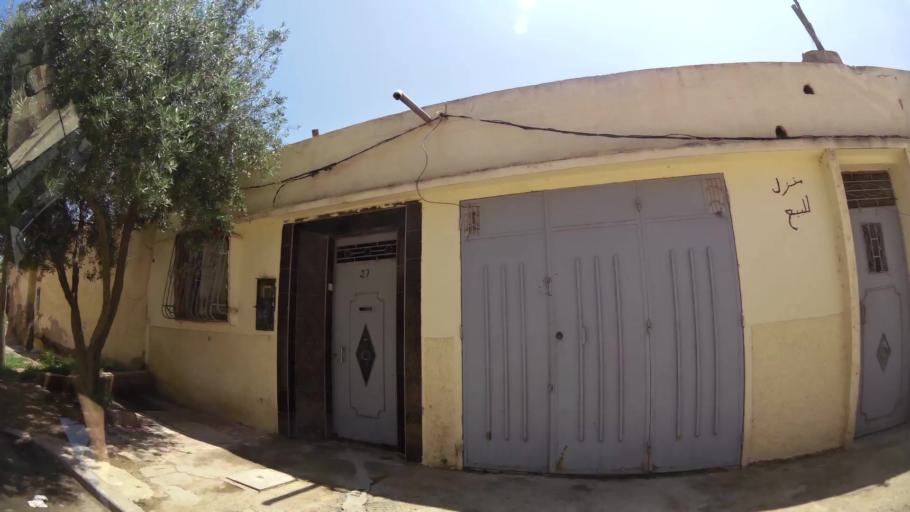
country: MA
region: Oriental
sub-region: Oujda-Angad
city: Oujda
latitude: 34.6852
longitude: -1.8975
